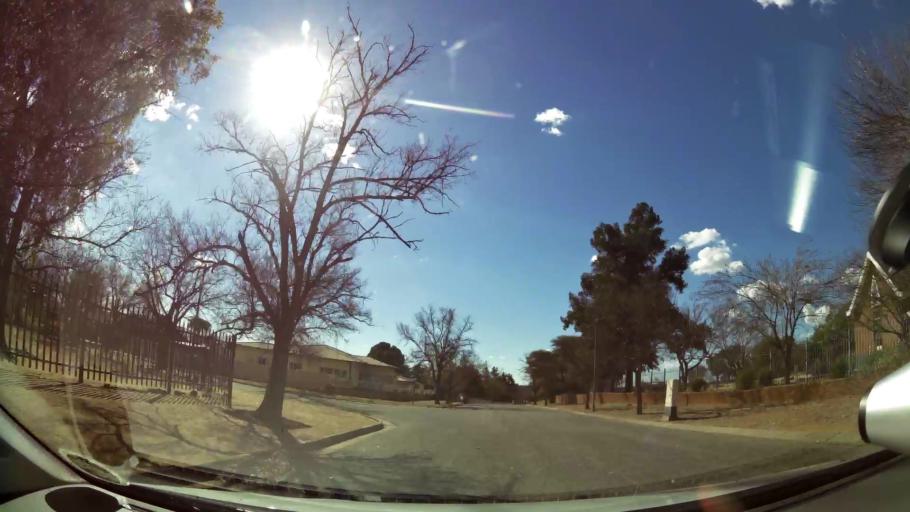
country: ZA
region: North-West
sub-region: Dr Kenneth Kaunda District Municipality
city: Klerksdorp
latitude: -26.8585
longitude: 26.6491
